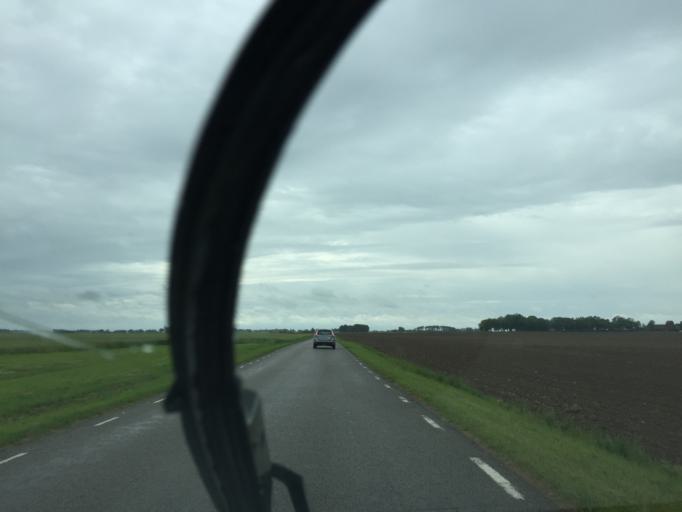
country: SE
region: OEstergoetland
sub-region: Vadstena Kommun
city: Vadstena
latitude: 58.4511
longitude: 14.8378
